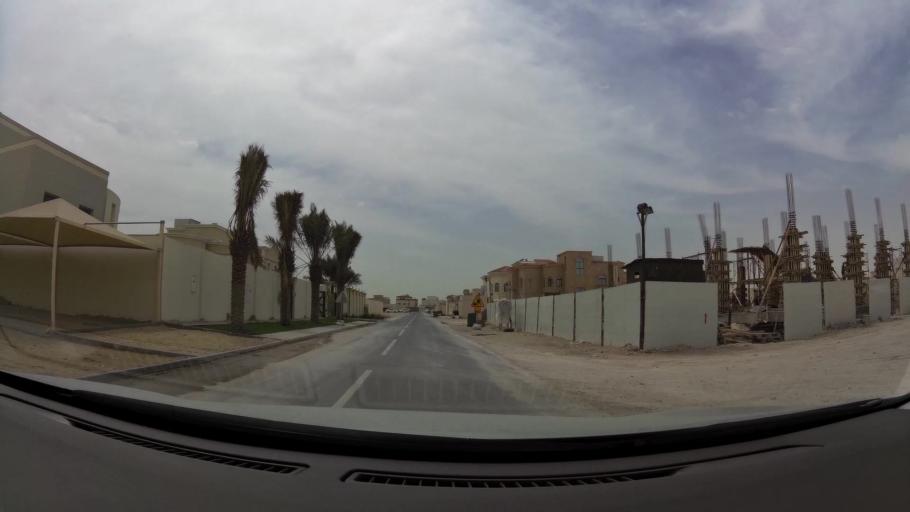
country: QA
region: Baladiyat ad Dawhah
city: Doha
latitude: 25.2198
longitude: 51.4658
